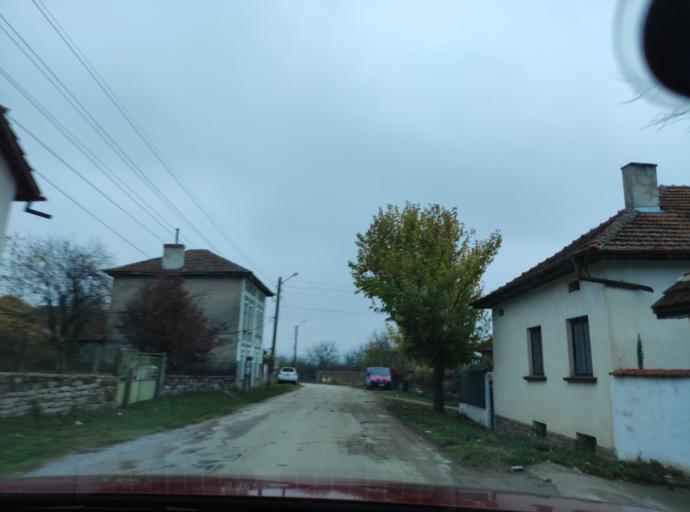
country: BG
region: Lovech
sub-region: Obshtina Yablanitsa
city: Yablanitsa
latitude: 43.0932
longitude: 24.0789
